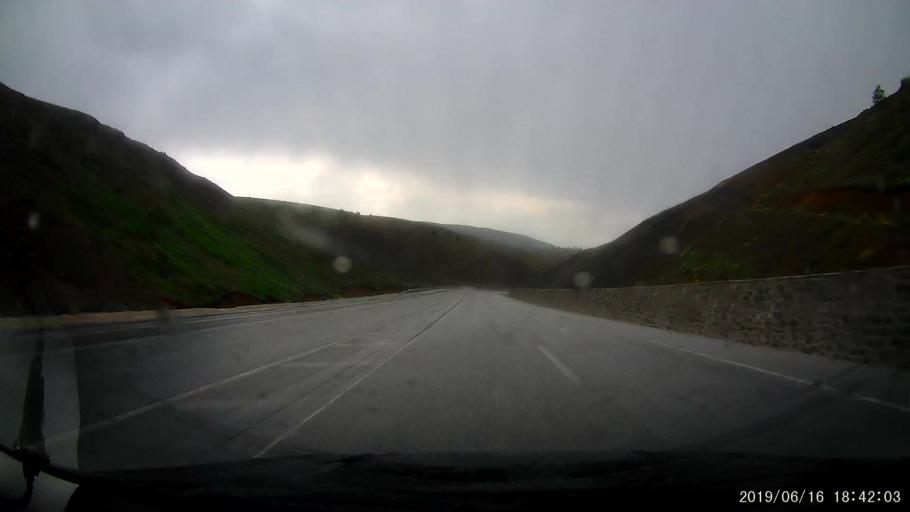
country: TR
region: Erzincan
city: Doganbeyli
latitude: 39.8720
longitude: 39.1167
